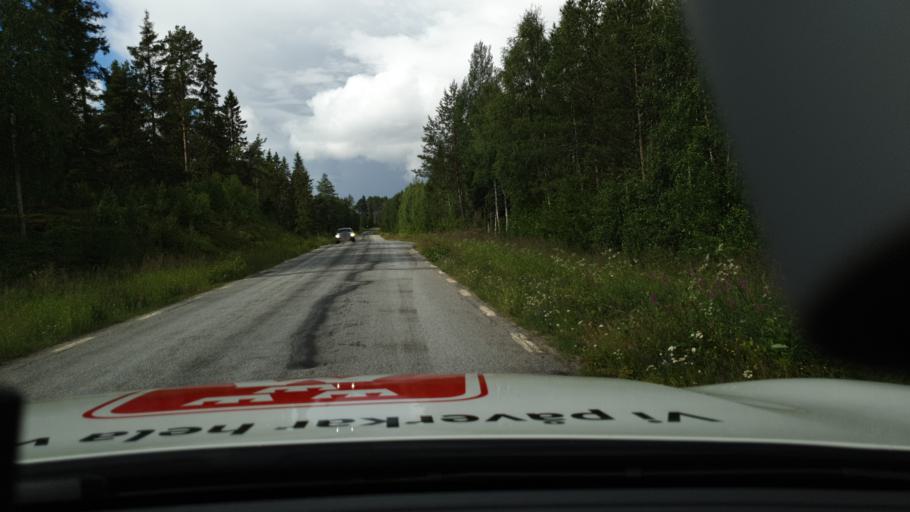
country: SE
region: Norrbotten
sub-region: Pitea Kommun
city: Rosvik
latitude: 65.4154
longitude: 21.7743
